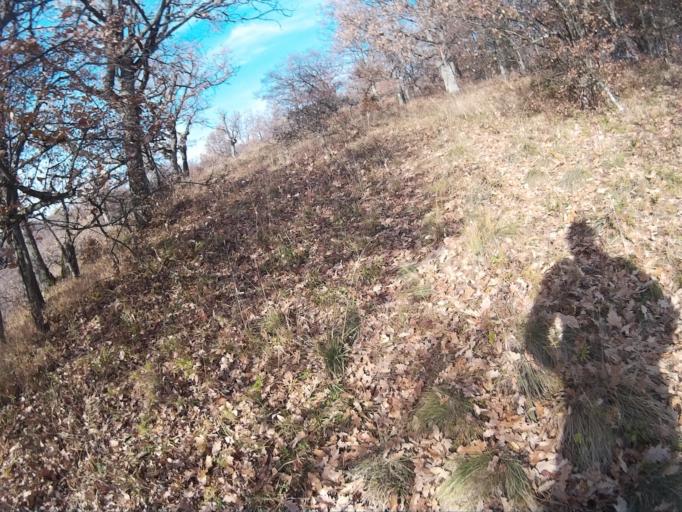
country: HU
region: Heves
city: Belapatfalva
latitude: 48.0342
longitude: 20.3913
